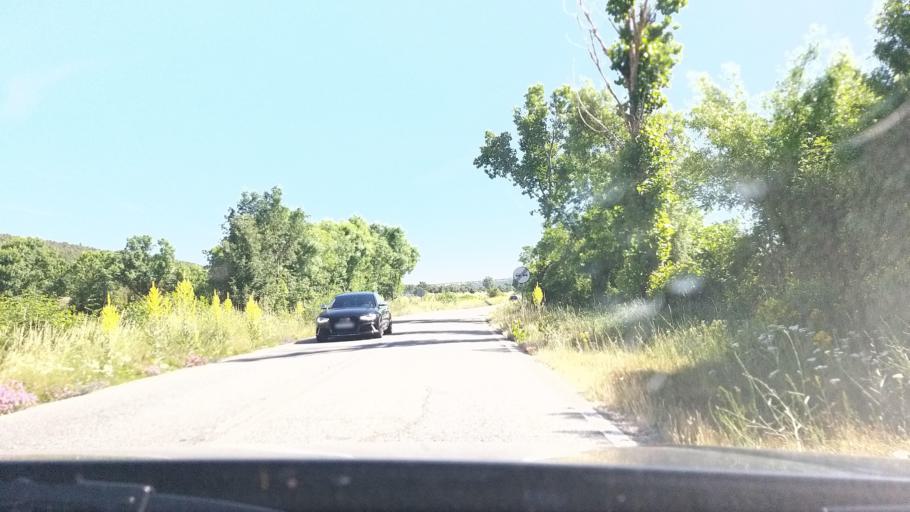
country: ES
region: Castille and Leon
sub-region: Provincia de Segovia
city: Arahuetes
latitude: 41.1313
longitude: -3.8384
